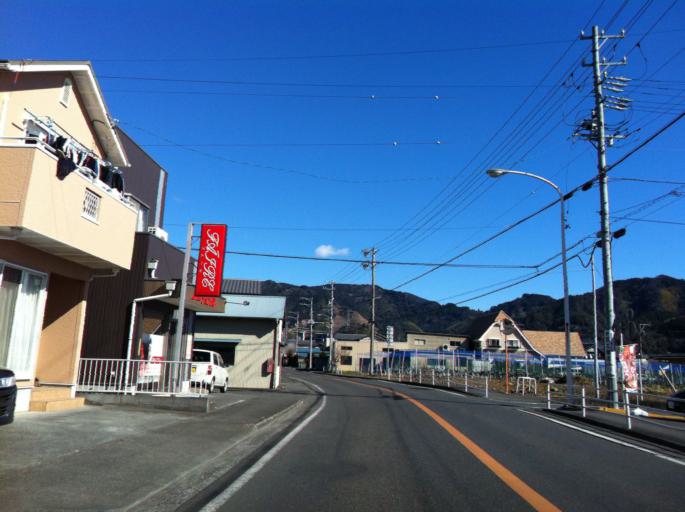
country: JP
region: Shizuoka
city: Shizuoka-shi
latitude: 35.0264
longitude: 138.3894
